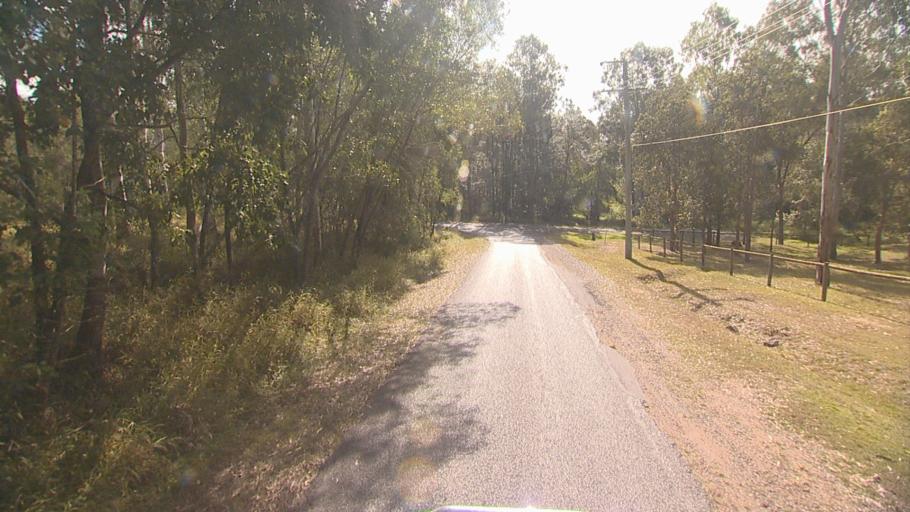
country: AU
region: Queensland
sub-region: Logan
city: North Maclean
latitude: -27.7807
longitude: 152.9937
